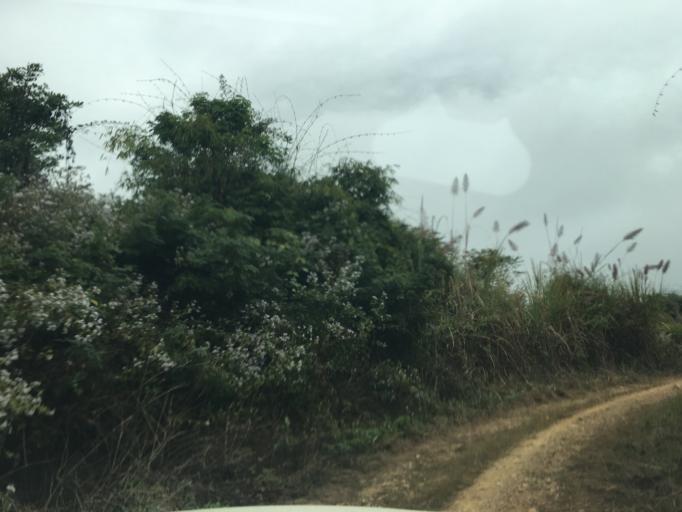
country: LA
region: Houaphan
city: Viengthong
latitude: 19.9391
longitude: 103.2978
